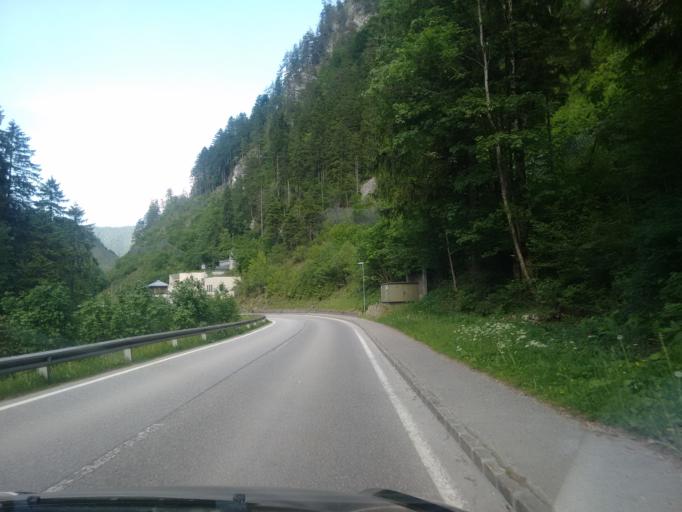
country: AT
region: Upper Austria
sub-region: Politischer Bezirk Kirchdorf an der Krems
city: Rossleithen
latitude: 47.7078
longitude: 14.1640
